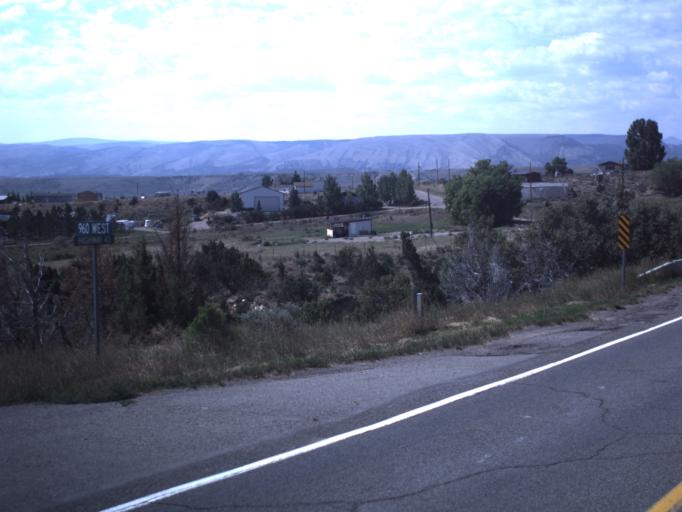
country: US
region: Utah
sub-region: Daggett County
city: Manila
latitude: 40.9808
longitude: -109.7458
